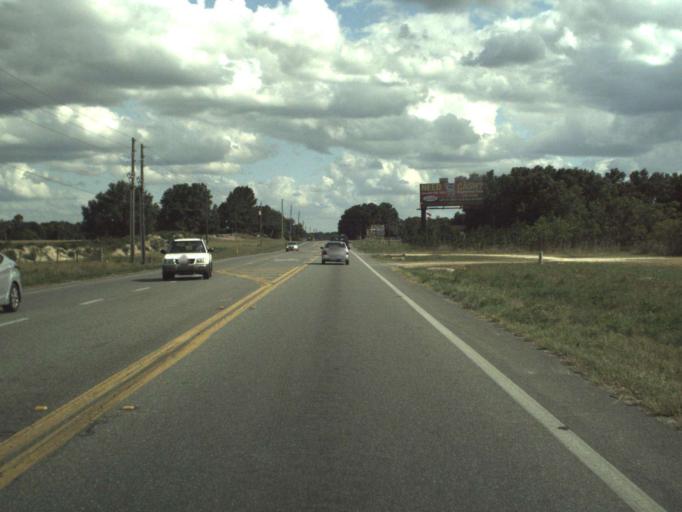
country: US
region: Florida
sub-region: Marion County
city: Belleview
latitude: 29.0850
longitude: -82.0536
